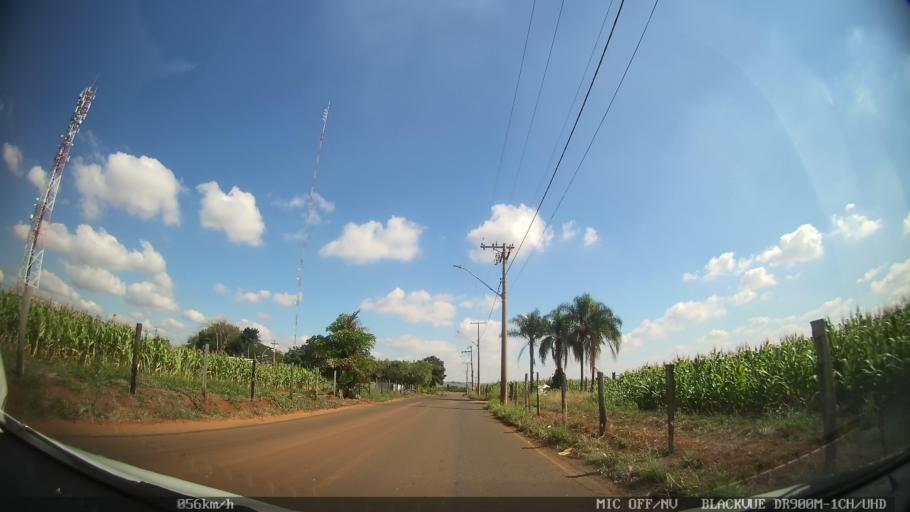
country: BR
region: Sao Paulo
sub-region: Hortolandia
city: Hortolandia
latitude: -22.8765
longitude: -47.2496
